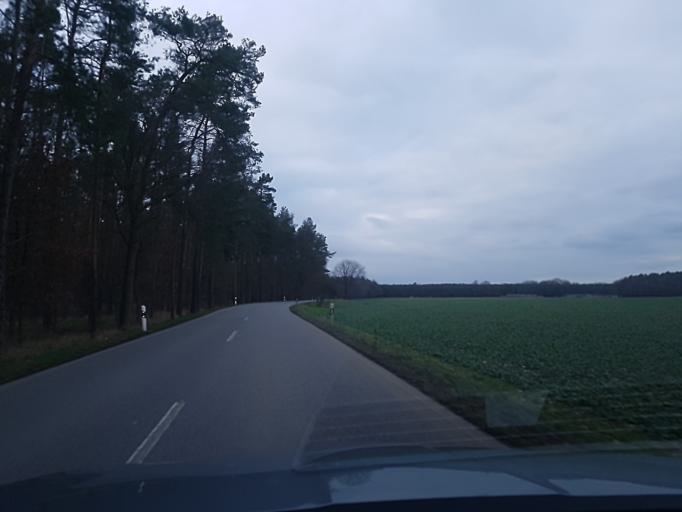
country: DE
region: Brandenburg
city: Finsterwalde
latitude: 51.6717
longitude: 13.6917
